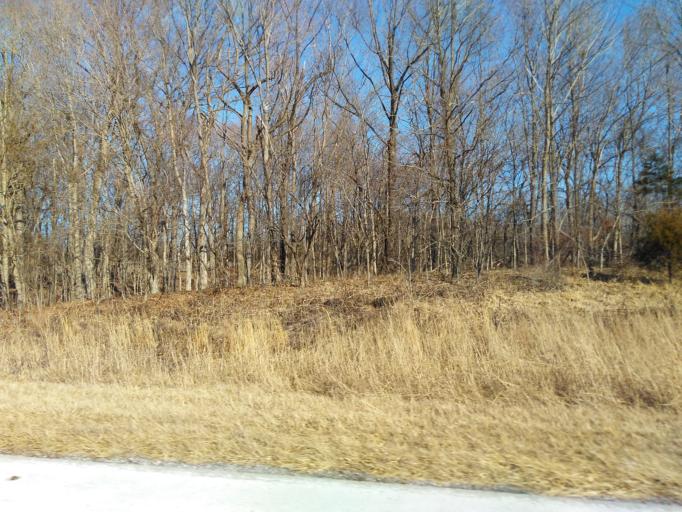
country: US
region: Illinois
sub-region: Johnson County
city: Vienna
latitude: 37.4616
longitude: -88.8897
